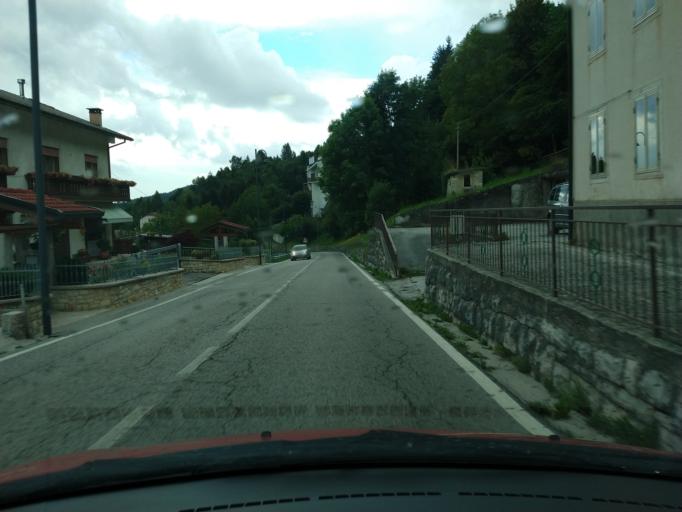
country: IT
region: Veneto
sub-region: Provincia di Vicenza
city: Tonezza del Cimone
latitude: 45.8557
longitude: 11.3456
